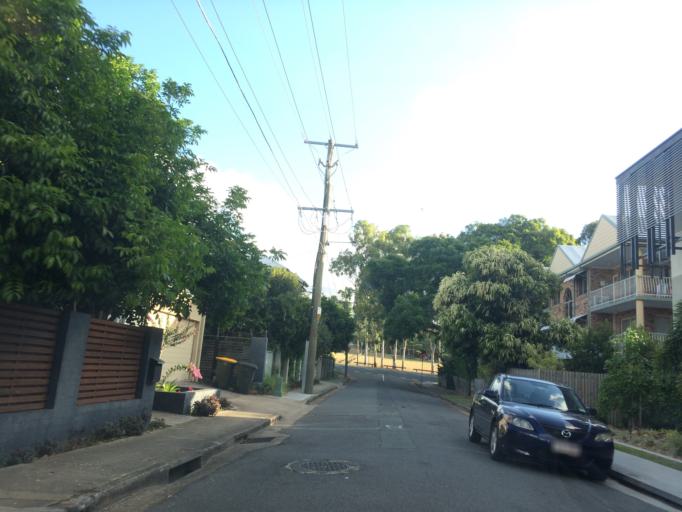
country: AU
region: Queensland
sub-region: Brisbane
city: Toowong
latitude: -27.4964
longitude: 152.9994
